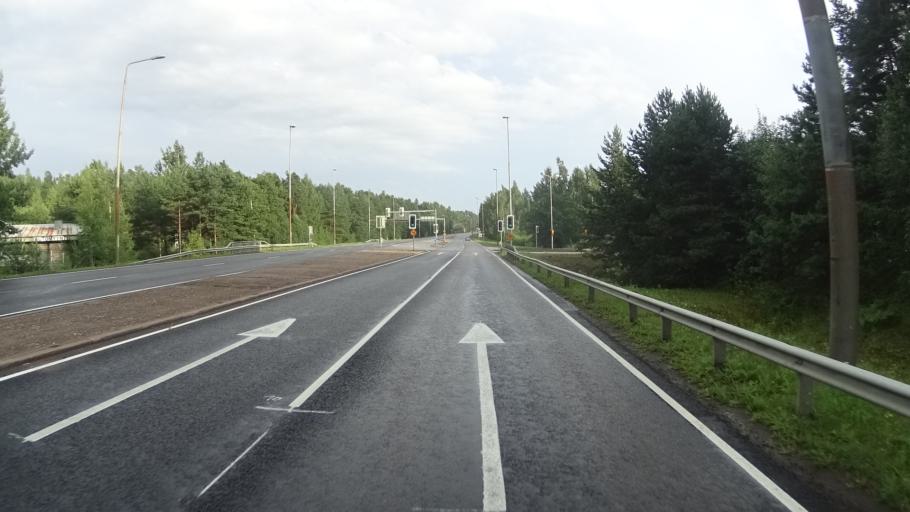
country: FI
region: Kymenlaakso
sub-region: Kotka-Hamina
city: Kotka
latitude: 60.4882
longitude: 26.9057
